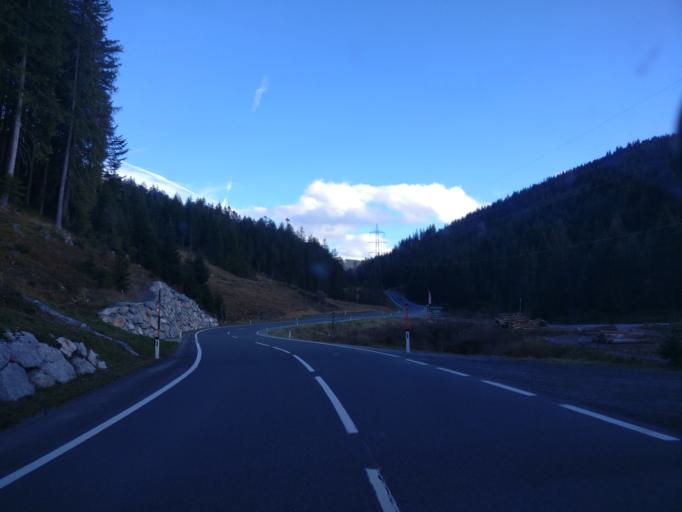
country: AT
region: Salzburg
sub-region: Politischer Bezirk Zell am See
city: Dienten am Hochkonig
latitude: 47.4002
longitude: 12.9940
